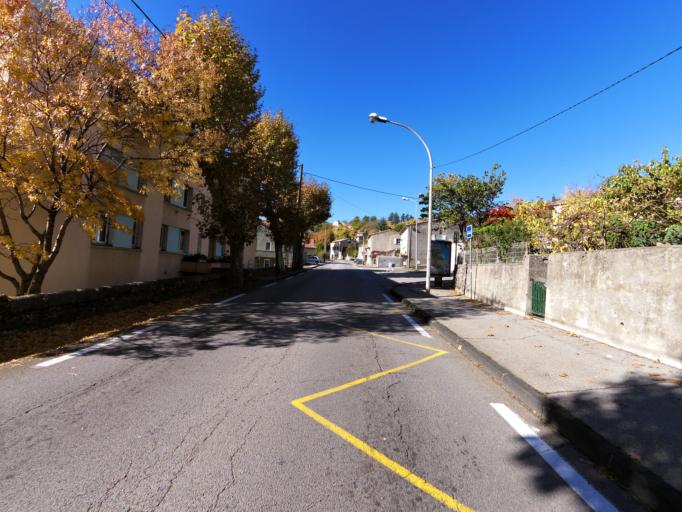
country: FR
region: Rhone-Alpes
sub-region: Departement de l'Ardeche
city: Privas
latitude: 44.7319
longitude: 4.5875
